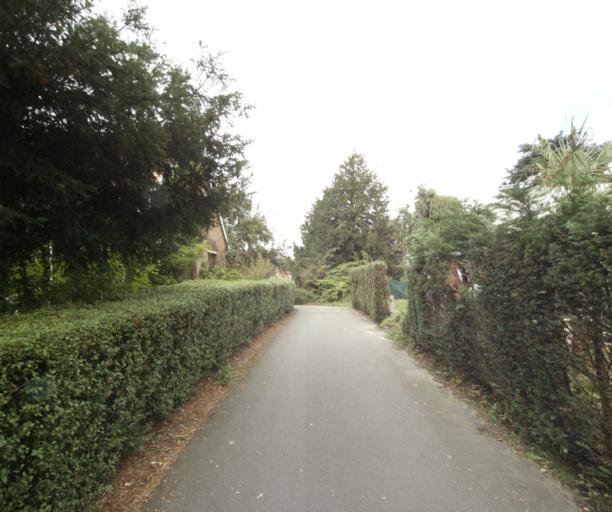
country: FR
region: Nord-Pas-de-Calais
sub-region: Departement du Nord
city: Villeneuve-d'Ascq
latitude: 50.6090
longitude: 3.1681
